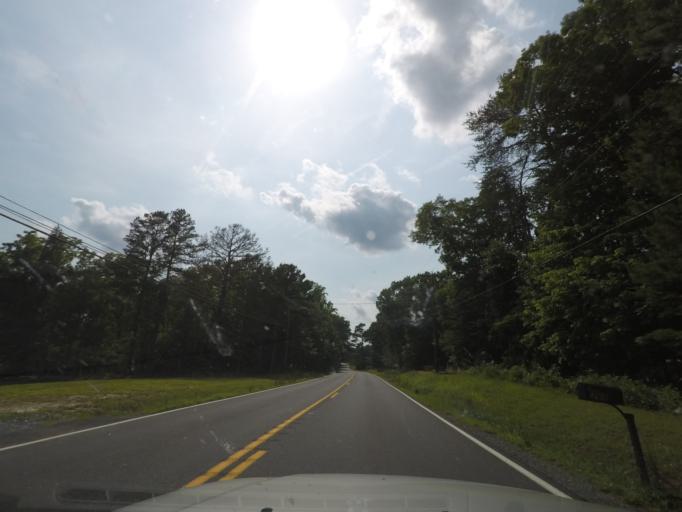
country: US
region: Virginia
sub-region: Fluvanna County
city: Weber City
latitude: 37.7551
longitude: -78.2763
